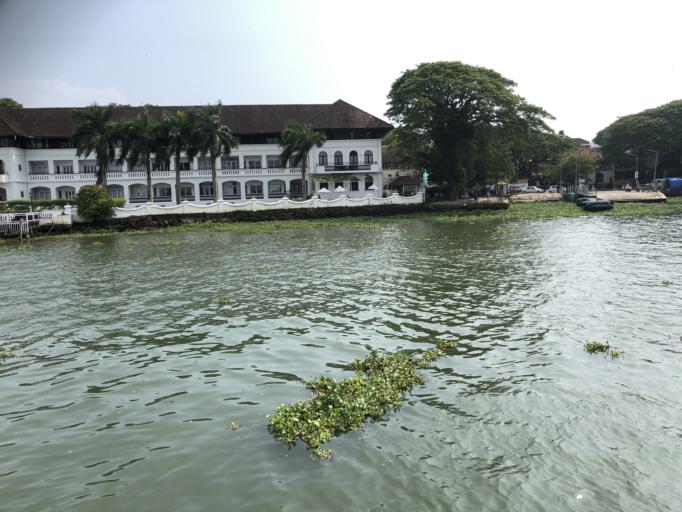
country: IN
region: Kerala
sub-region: Ernakulam
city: Cochin
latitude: 9.9695
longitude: 76.2453
